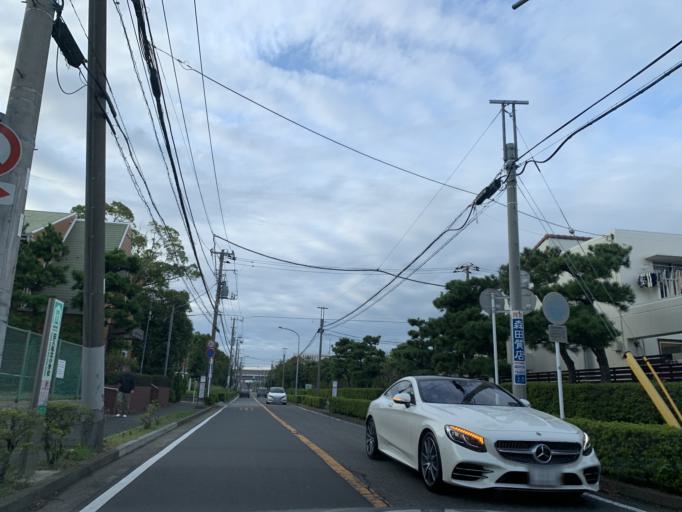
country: JP
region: Tokyo
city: Urayasu
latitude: 35.6513
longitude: 139.9185
